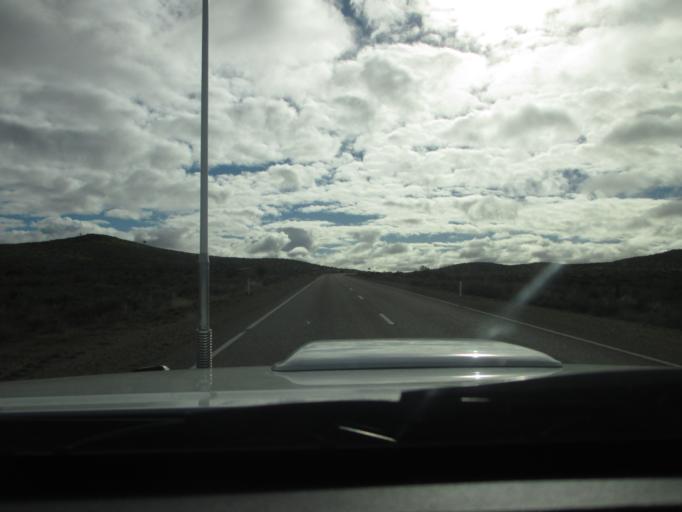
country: AU
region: South Australia
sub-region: Flinders Ranges
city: Quorn
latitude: -32.2737
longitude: 138.4963
